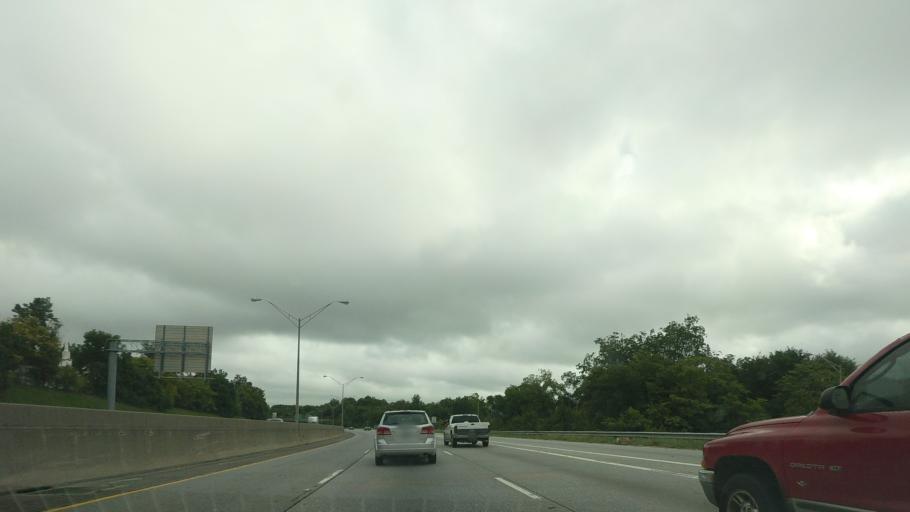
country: US
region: Georgia
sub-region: Bibb County
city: Macon
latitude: 32.8440
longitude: -83.6435
